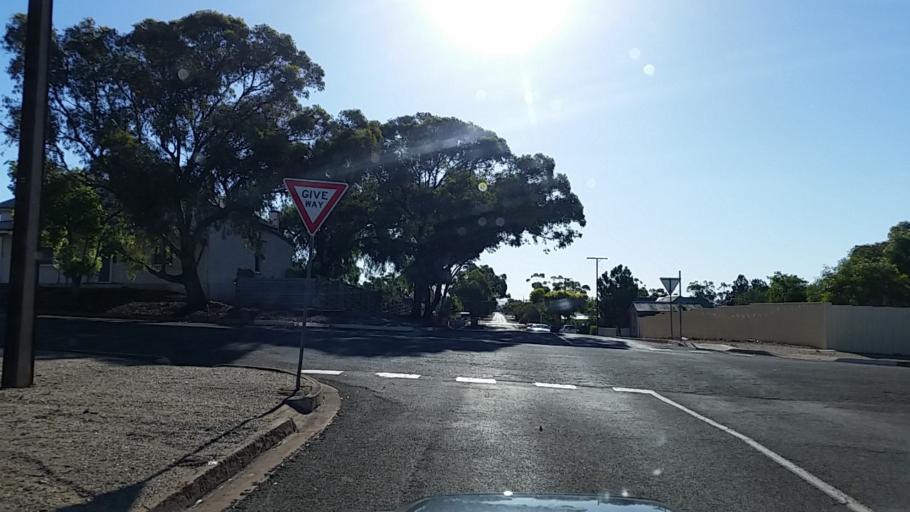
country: AU
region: South Australia
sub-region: Peterborough
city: Peterborough
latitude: -32.9771
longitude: 138.8343
